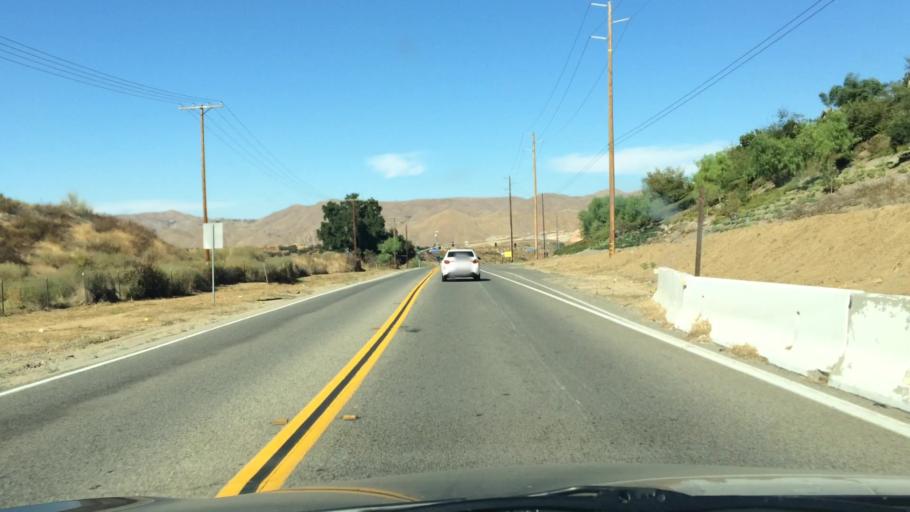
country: US
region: California
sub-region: Riverside County
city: Lake Elsinore
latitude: 33.7029
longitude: -117.3897
